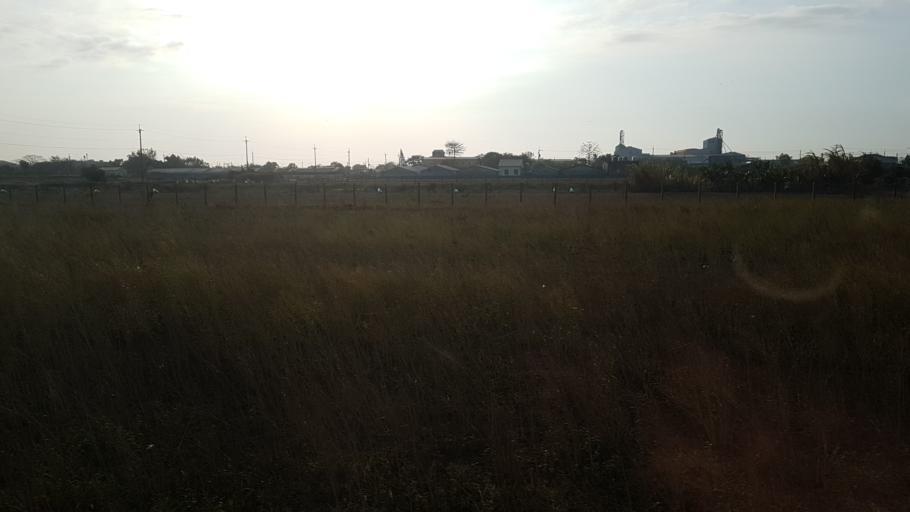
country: TW
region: Taiwan
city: Xinying
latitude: 23.3452
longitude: 120.3591
